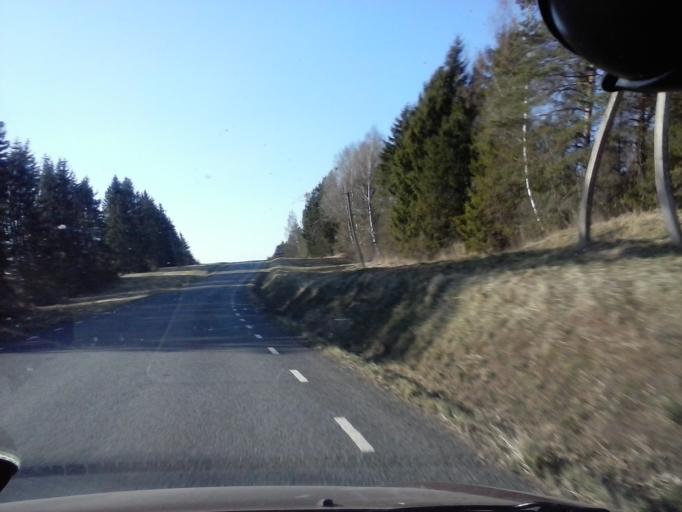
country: EE
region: Tartu
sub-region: UElenurme vald
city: Ulenurme
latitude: 58.1672
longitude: 26.8401
